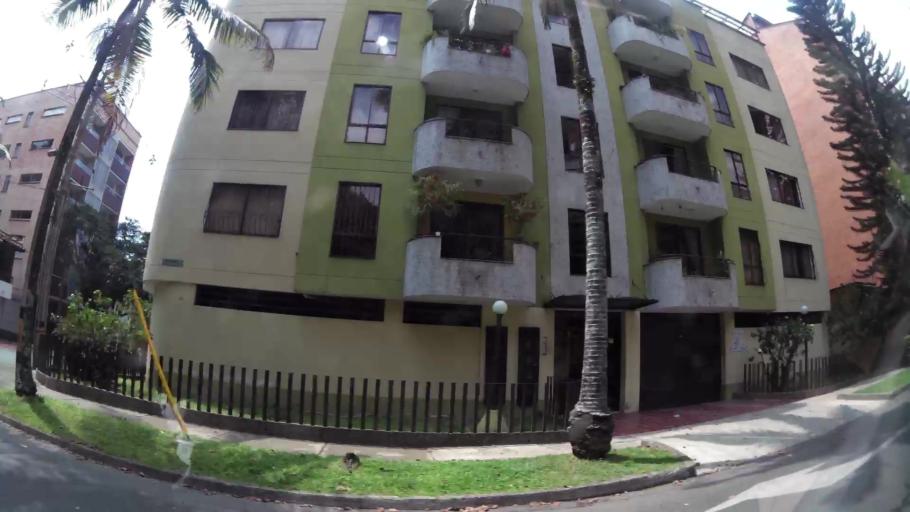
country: CO
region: Antioquia
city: Envigado
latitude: 6.1745
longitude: -75.5892
